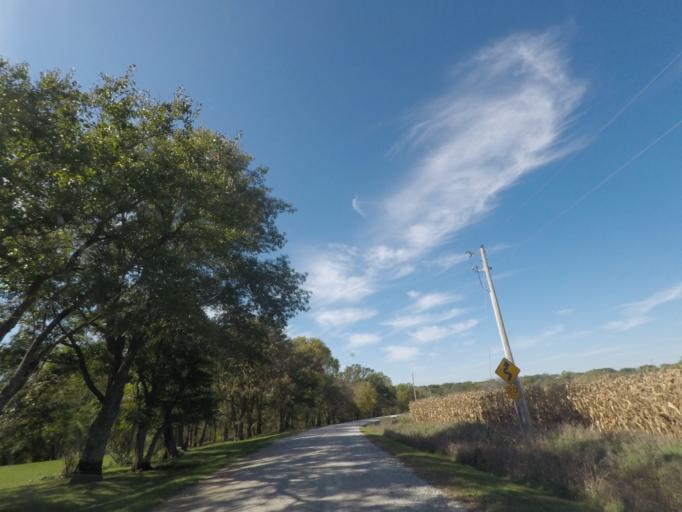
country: US
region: Iowa
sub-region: Story County
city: Nevada
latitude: 42.0121
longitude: -93.3484
